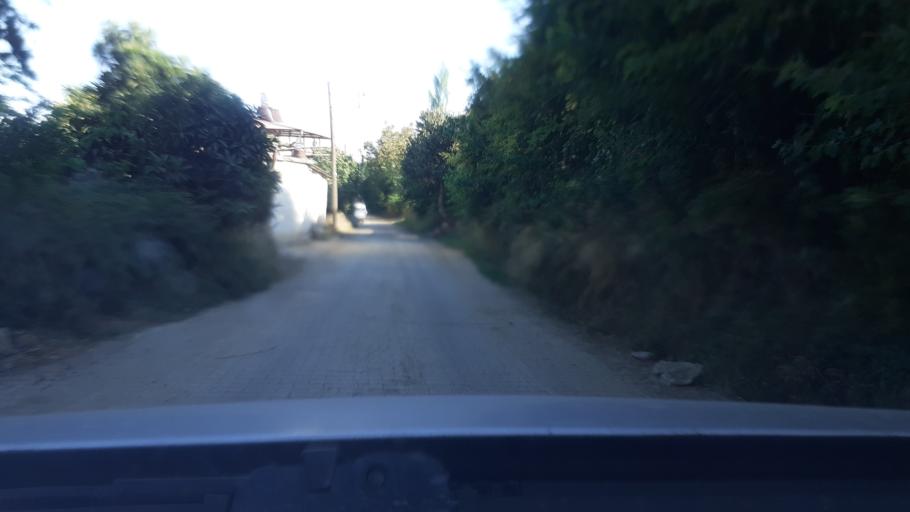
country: TR
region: Hatay
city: Kirikhan
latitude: 36.4884
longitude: 36.3005
